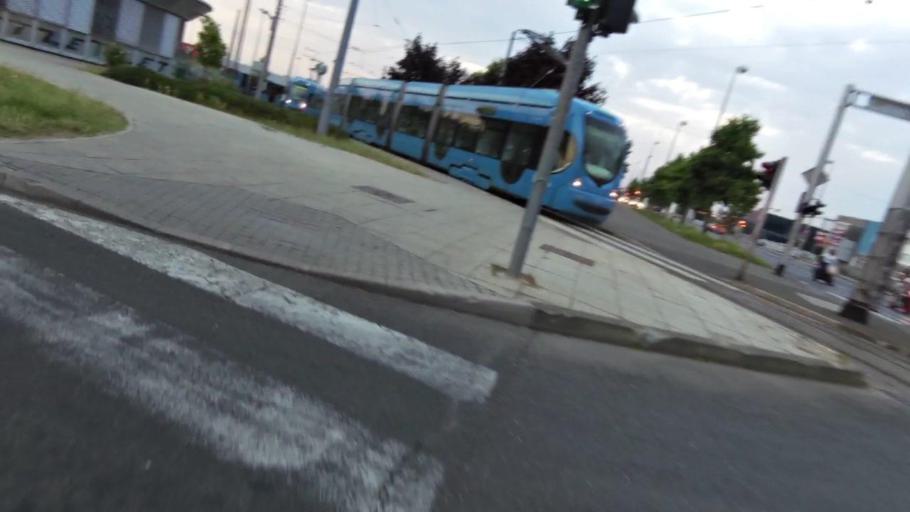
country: HR
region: Grad Zagreb
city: Dubrava
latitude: 45.8280
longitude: 16.0764
